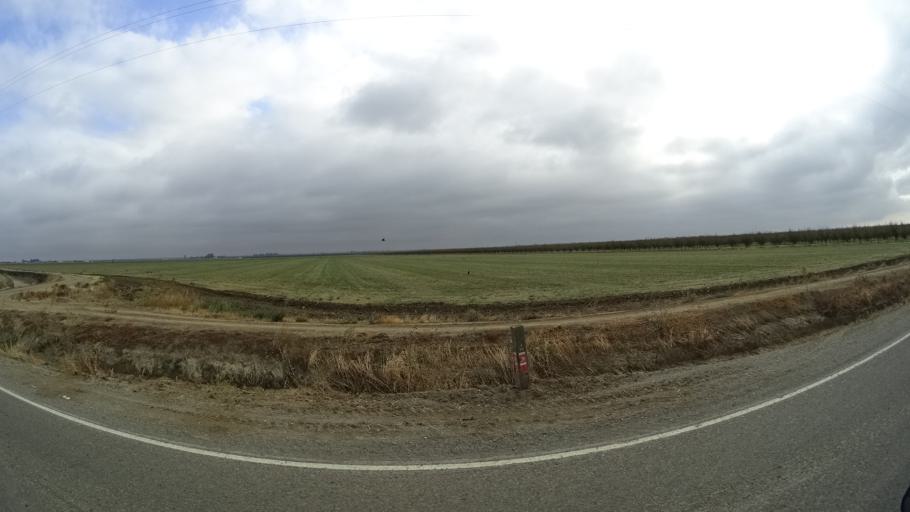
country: US
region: California
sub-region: Yolo County
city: Esparto
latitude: 38.7342
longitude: -122.0453
